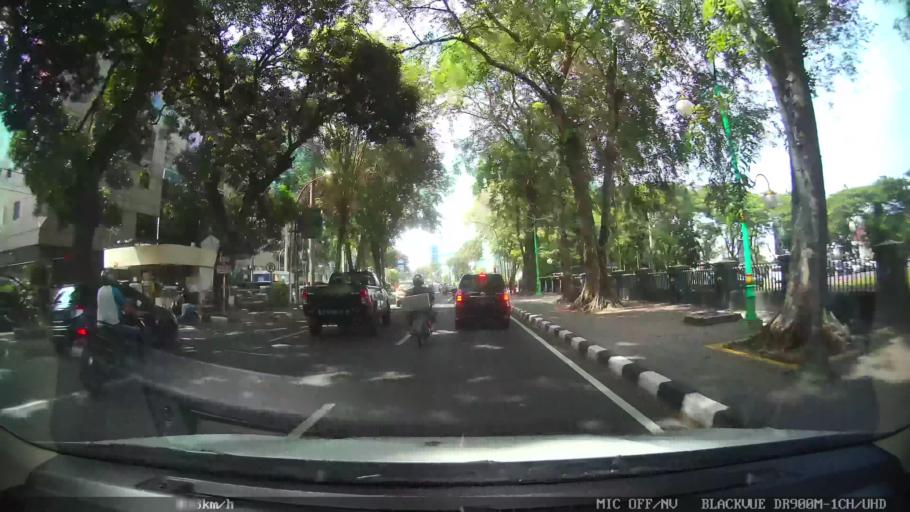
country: ID
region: North Sumatra
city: Medan
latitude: 3.5875
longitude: 98.6741
